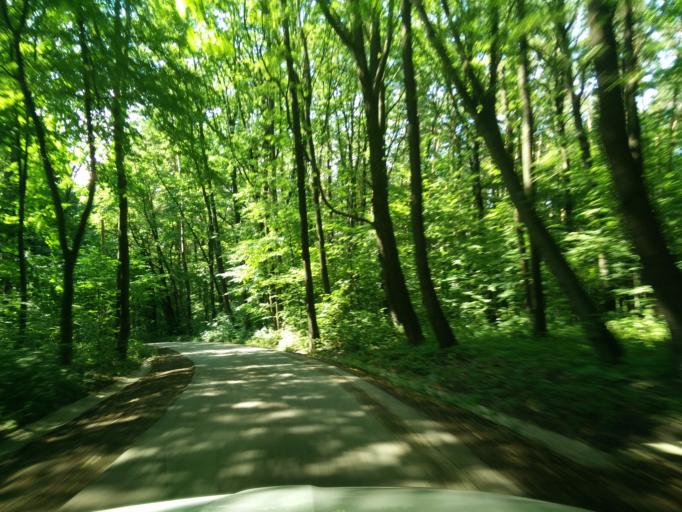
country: SK
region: Nitriansky
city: Prievidza
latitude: 48.7447
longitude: 18.6377
